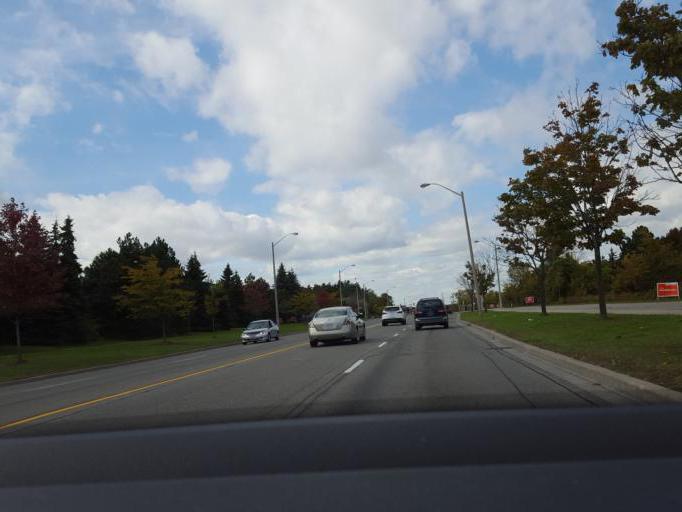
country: CA
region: Ontario
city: Scarborough
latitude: 43.8170
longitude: -79.2121
